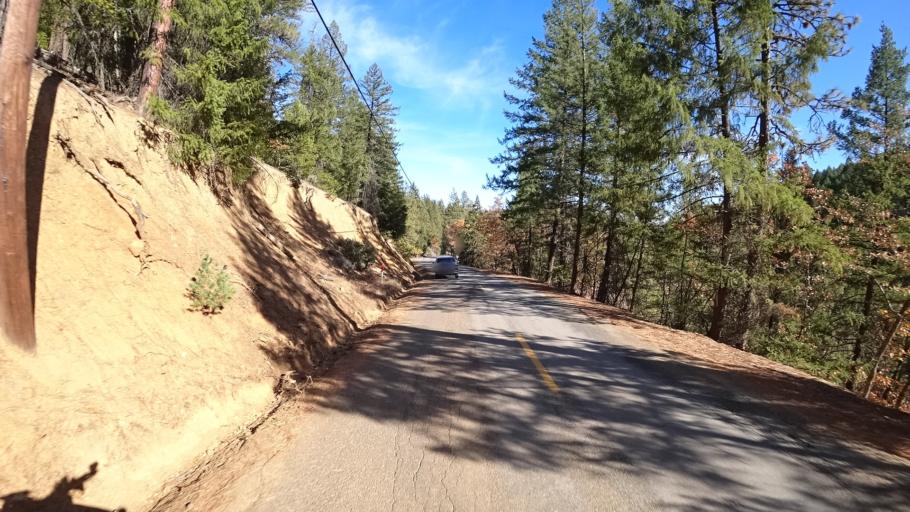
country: US
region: California
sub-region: Siskiyou County
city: Yreka
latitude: 41.7285
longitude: -122.7120
